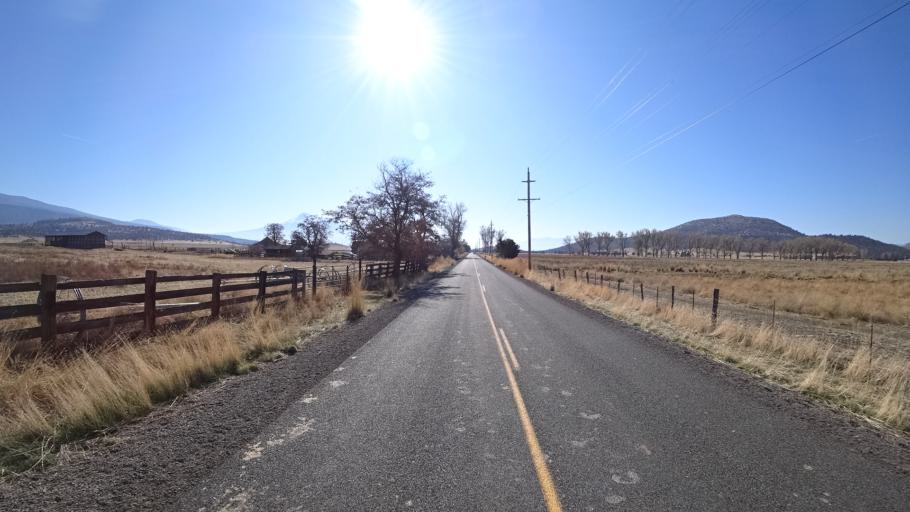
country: US
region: California
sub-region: Siskiyou County
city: Montague
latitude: 41.6880
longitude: -122.3697
